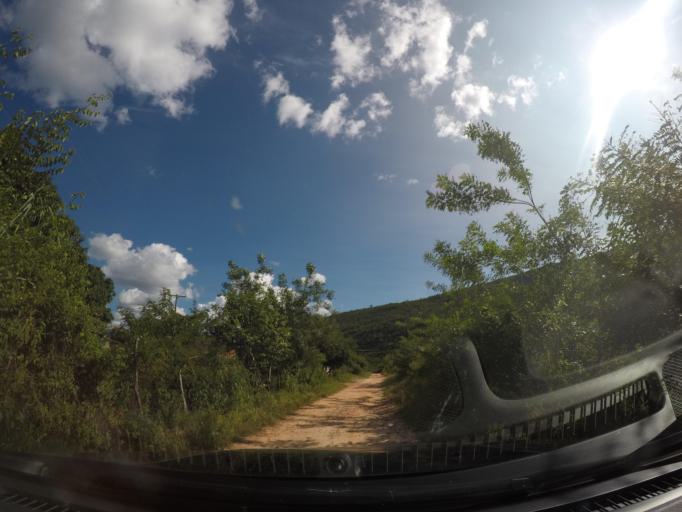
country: BR
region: Bahia
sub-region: Livramento Do Brumado
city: Livramento do Brumado
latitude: -13.2166
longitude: -41.6069
